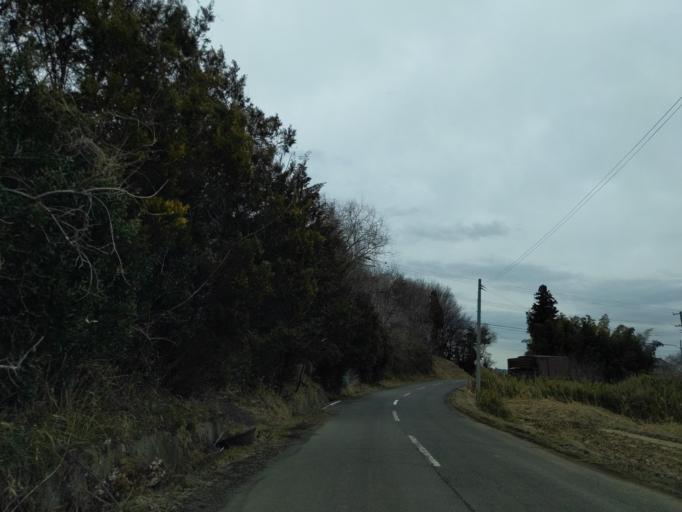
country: JP
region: Fukushima
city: Motomiya
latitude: 37.4678
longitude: 140.3963
